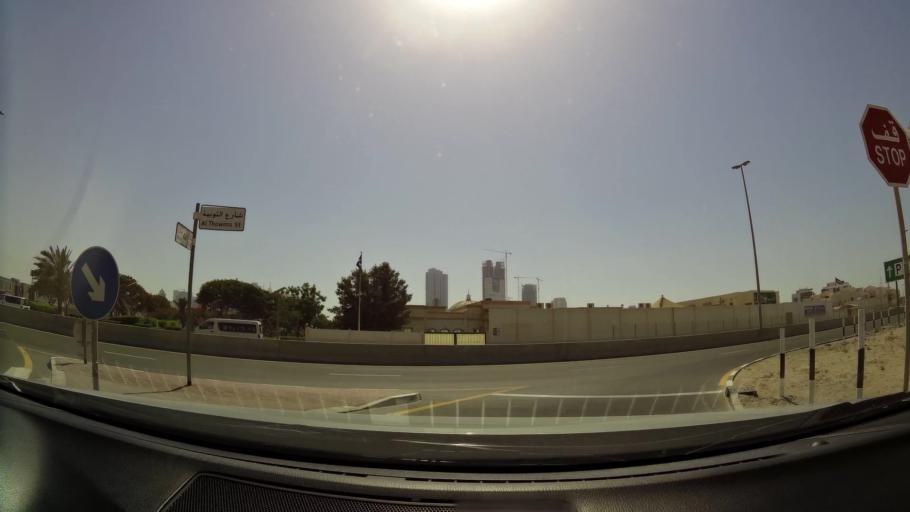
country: AE
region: Dubai
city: Dubai
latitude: 25.1080
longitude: 55.1902
